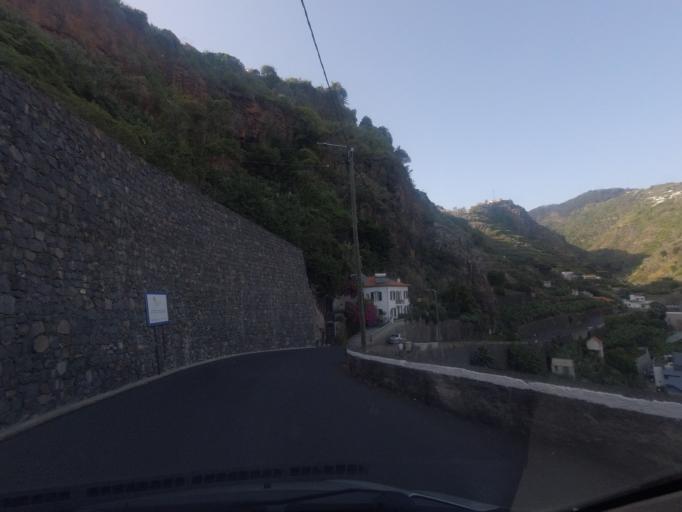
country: PT
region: Madeira
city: Ponta do Sol
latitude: 32.6837
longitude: -17.1016
